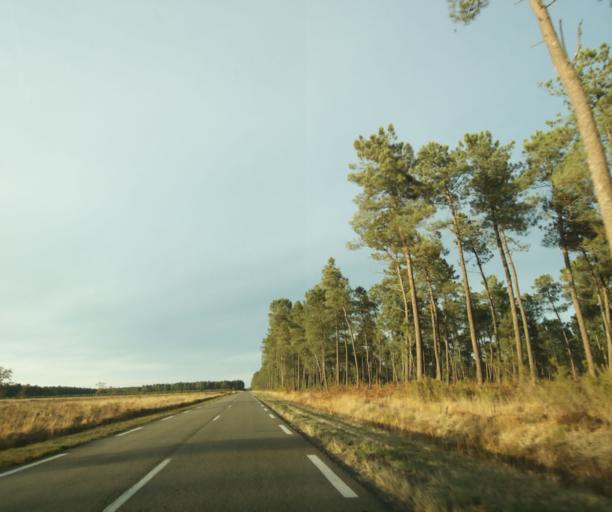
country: FR
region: Aquitaine
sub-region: Departement des Landes
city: Roquefort
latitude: 44.1708
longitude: -0.1395
